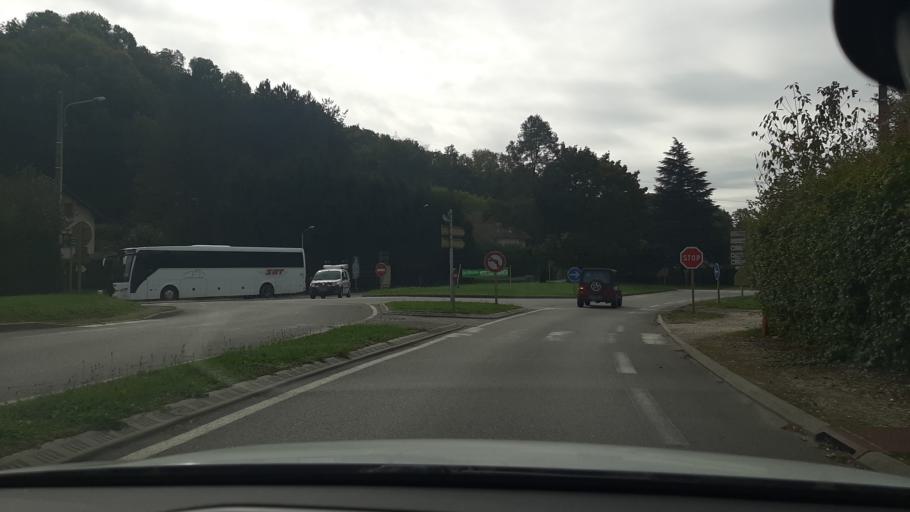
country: FR
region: Rhone-Alpes
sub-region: Departement de la Savoie
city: Montmelian
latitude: 45.4603
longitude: 6.0515
